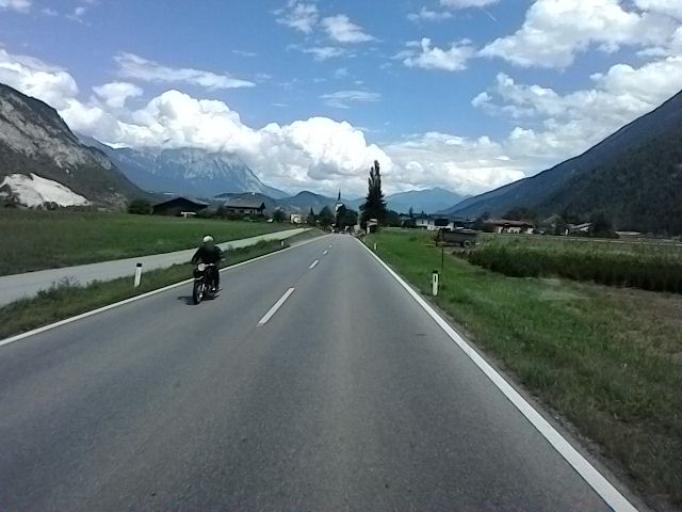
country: AT
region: Tyrol
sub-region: Politischer Bezirk Imst
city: Silz
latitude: 47.2626
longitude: 10.9186
